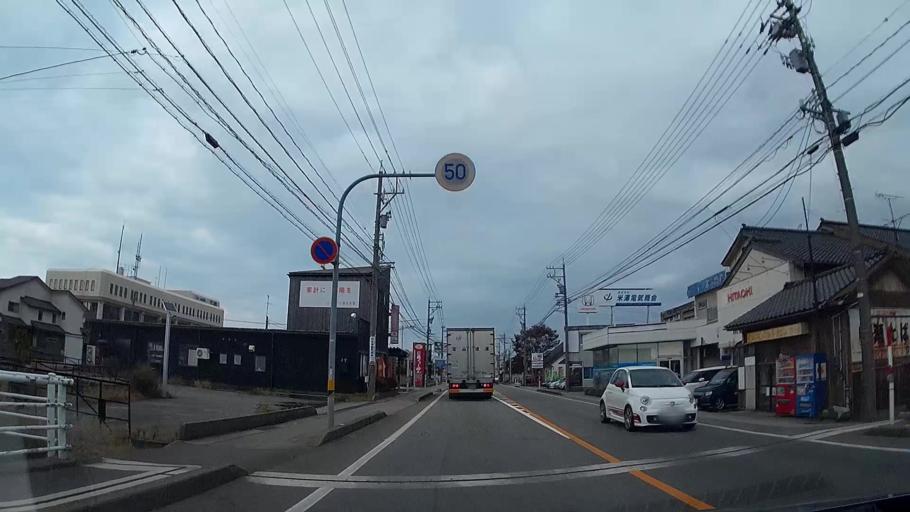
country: JP
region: Toyama
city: Nyuzen
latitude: 36.9324
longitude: 137.5020
